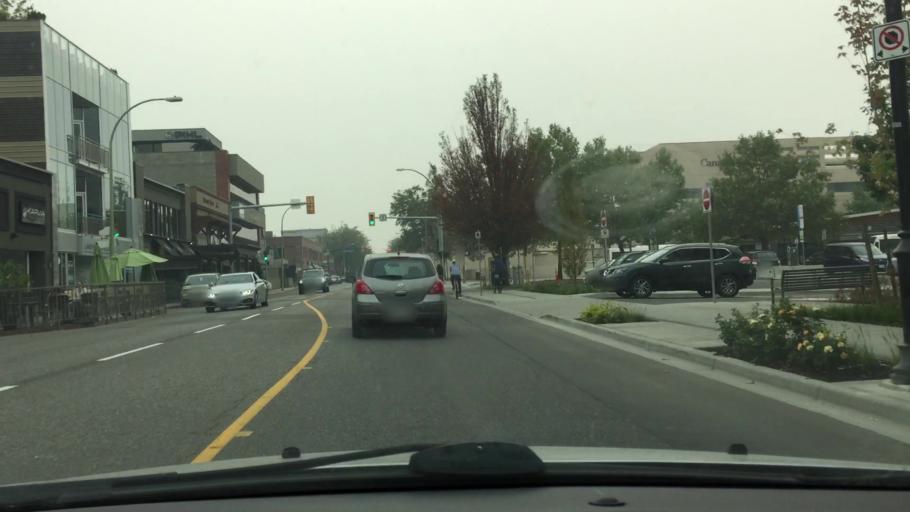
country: CA
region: British Columbia
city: Kelowna
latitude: 49.8881
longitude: -119.4936
